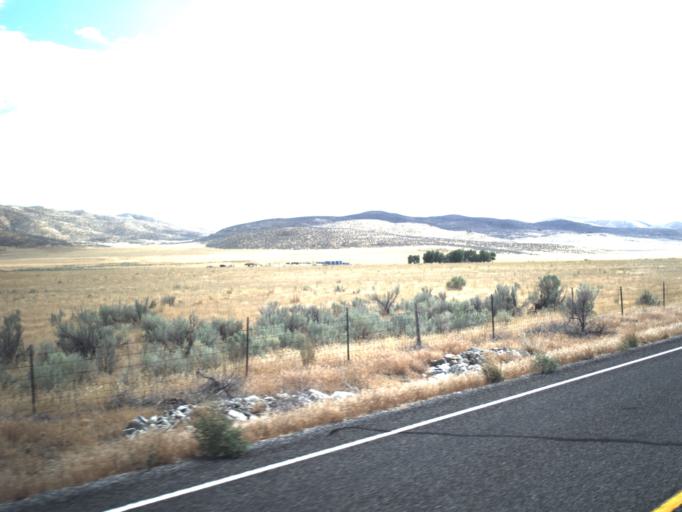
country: US
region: Utah
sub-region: Box Elder County
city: Garland
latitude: 41.8059
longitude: -112.4165
